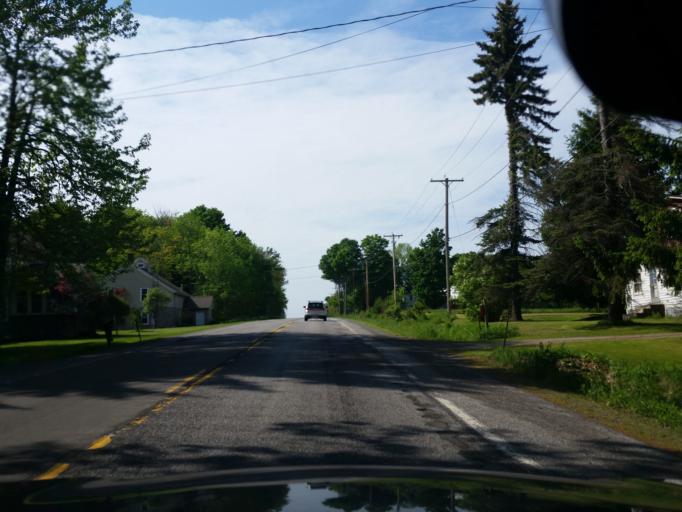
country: US
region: New York
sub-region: Chautauqua County
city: Mayville
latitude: 42.2080
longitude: -79.4241
